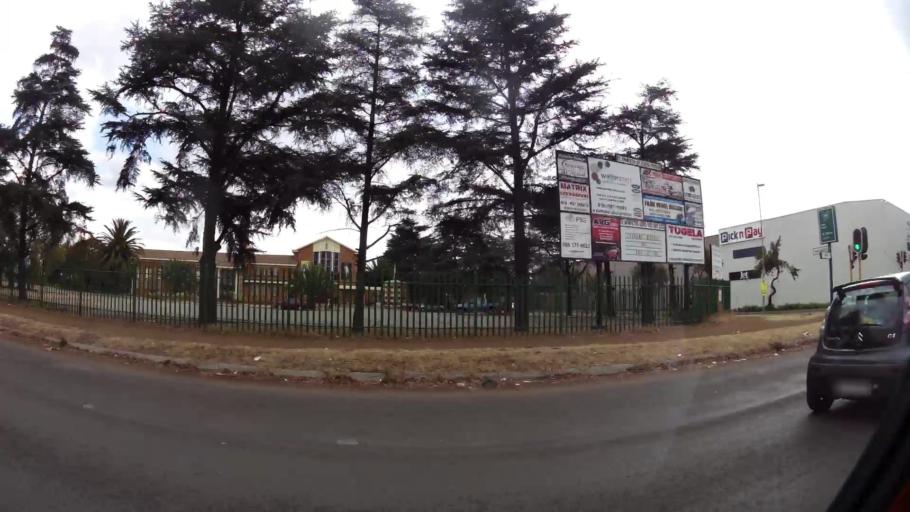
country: ZA
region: Gauteng
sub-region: Sedibeng District Municipality
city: Vanderbijlpark
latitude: -26.7106
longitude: 27.8251
